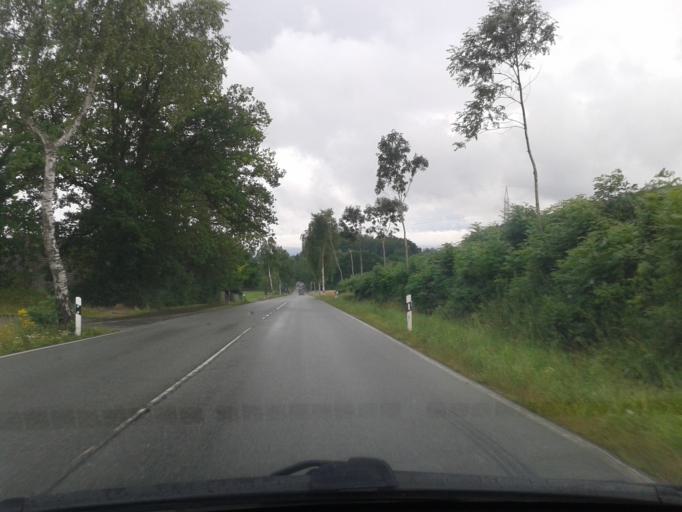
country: DE
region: North Rhine-Westphalia
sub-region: Regierungsbezirk Detmold
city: Detmold
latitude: 51.9769
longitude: 8.8961
